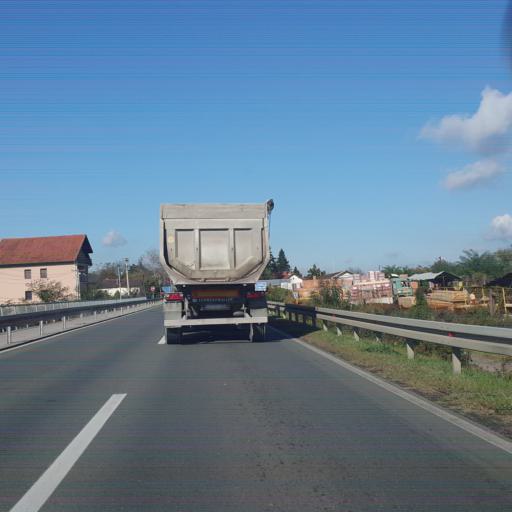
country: RS
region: Central Serbia
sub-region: Raski Okrug
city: Vrnjacka Banja
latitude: 43.6378
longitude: 20.9287
